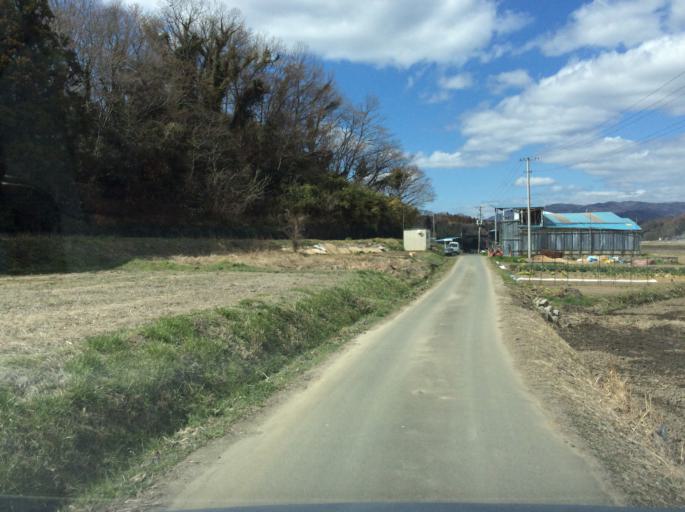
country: JP
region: Fukushima
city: Iwaki
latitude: 37.0857
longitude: 140.9473
